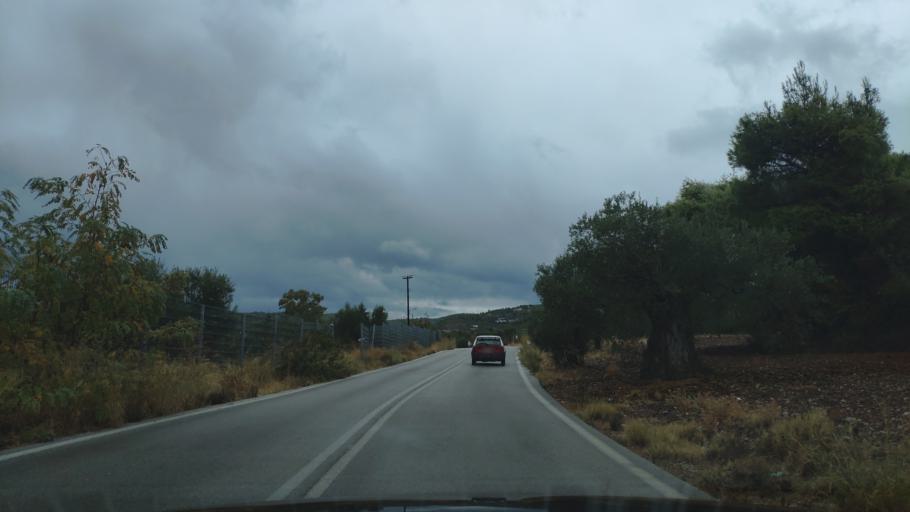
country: GR
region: Peloponnese
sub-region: Nomos Korinthias
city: Perachora
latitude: 38.0134
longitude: 22.9457
